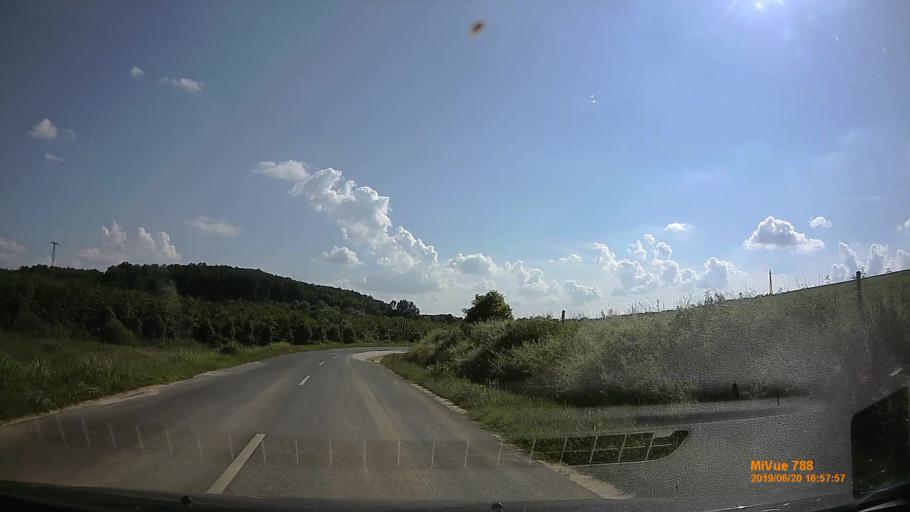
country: HU
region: Baranya
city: Buekkoesd
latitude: 46.1397
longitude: 18.0576
